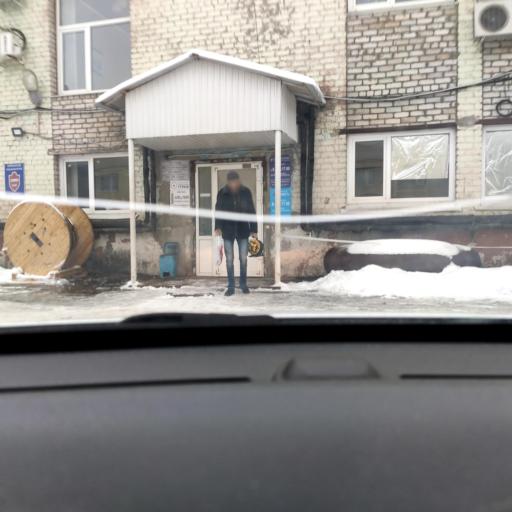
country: RU
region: Voronezj
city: Voronezh
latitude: 51.6942
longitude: 39.2728
